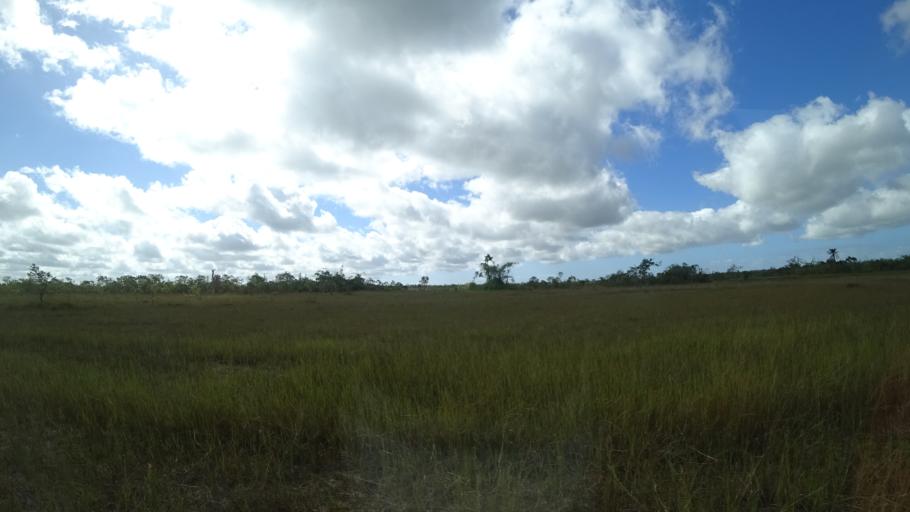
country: MZ
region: Sofala
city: Dondo
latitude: -19.5831
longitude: 35.0868
